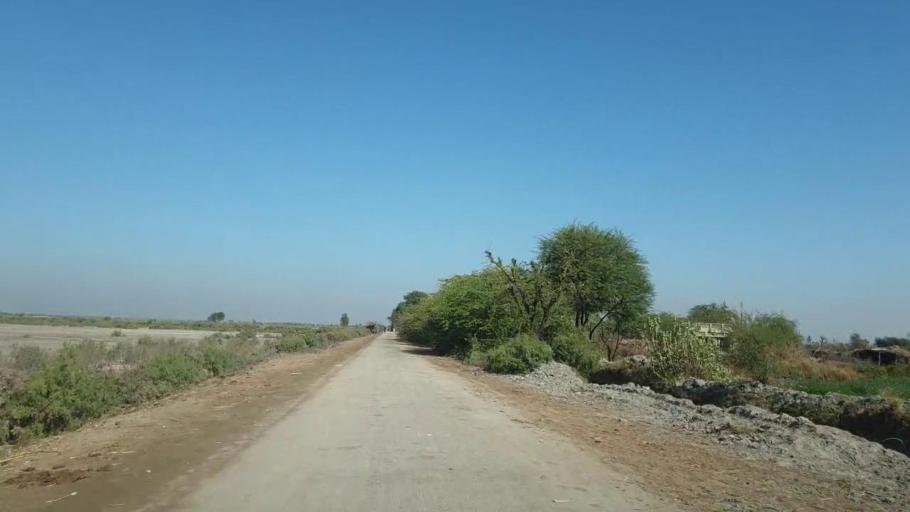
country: PK
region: Sindh
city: Mirpur Khas
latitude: 25.6171
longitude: 69.0240
